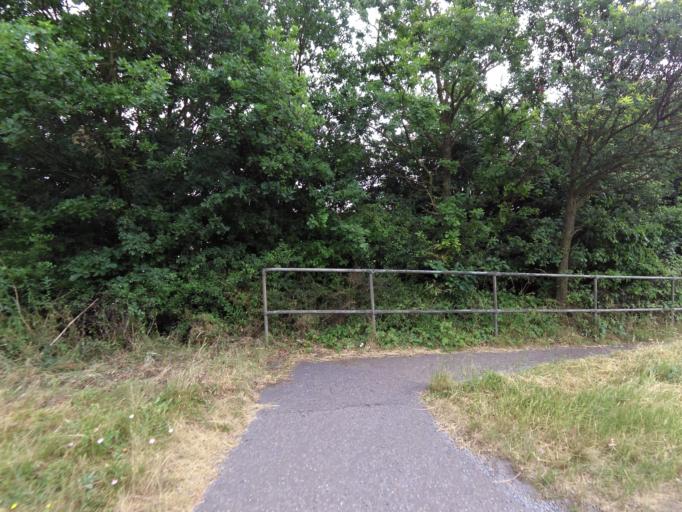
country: GB
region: England
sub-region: Norfolk
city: Harleston
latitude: 52.4035
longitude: 1.3155
